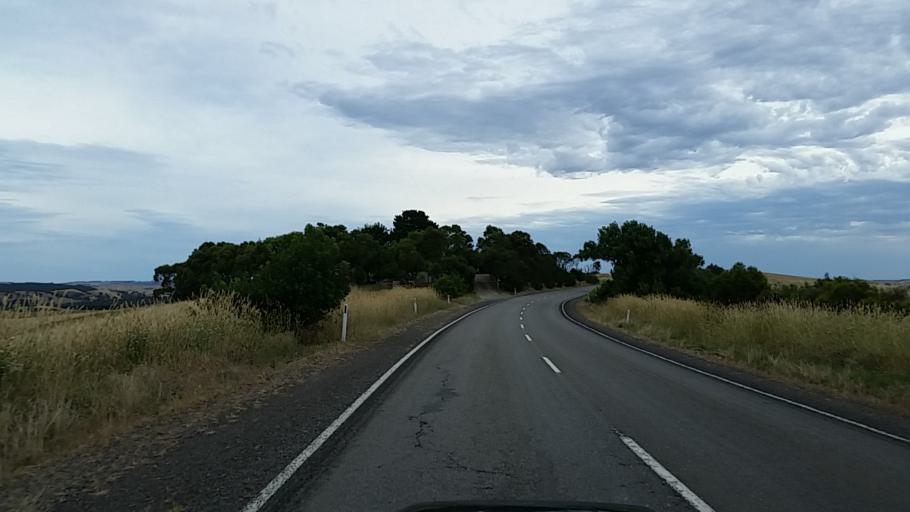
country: AU
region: South Australia
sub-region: Onkaparinga
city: Port Willunga
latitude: -35.3807
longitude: 138.4393
